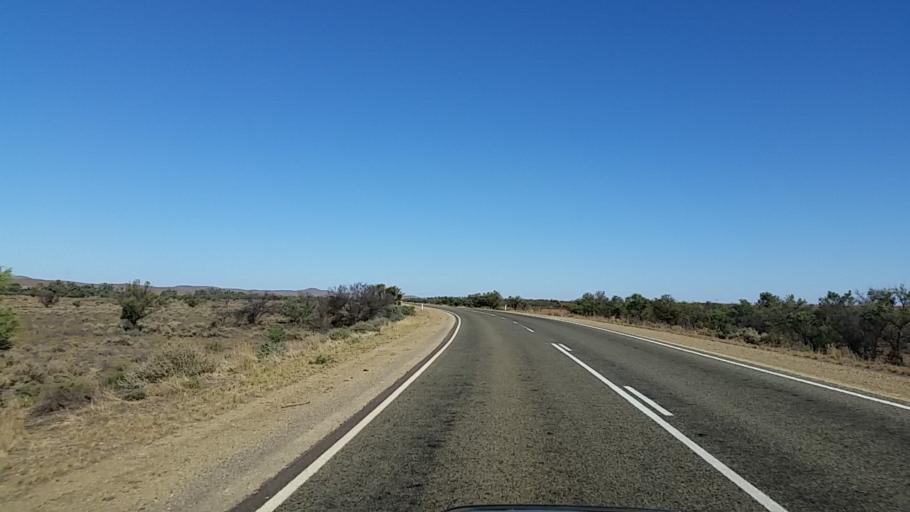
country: AU
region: South Australia
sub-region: Flinders Ranges
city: Quorn
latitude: -32.3865
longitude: 138.5034
